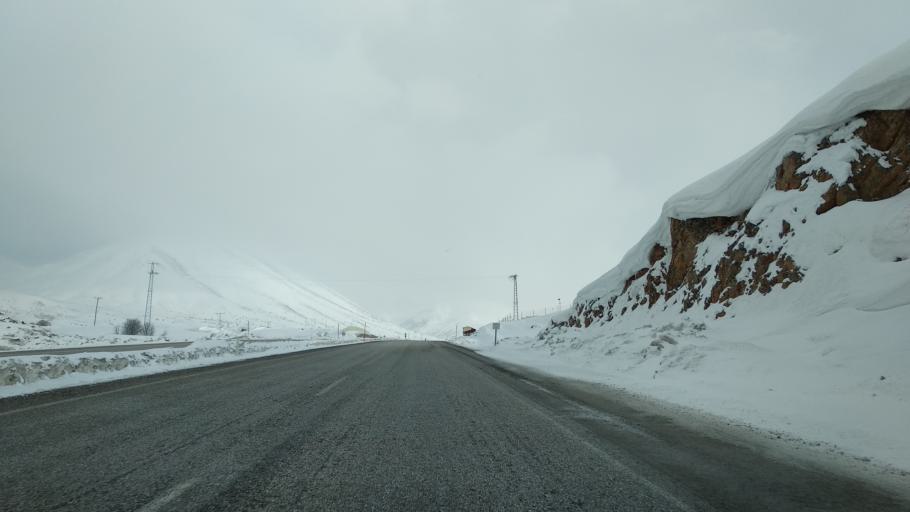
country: TR
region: Kahramanmaras
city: Goksun
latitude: 38.2047
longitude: 36.4398
